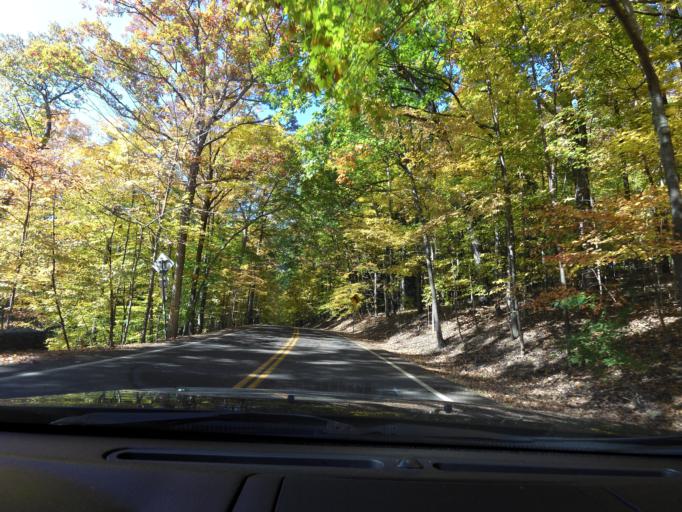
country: US
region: New York
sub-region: Wyoming County
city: Castile
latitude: 42.6134
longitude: -78.0140
